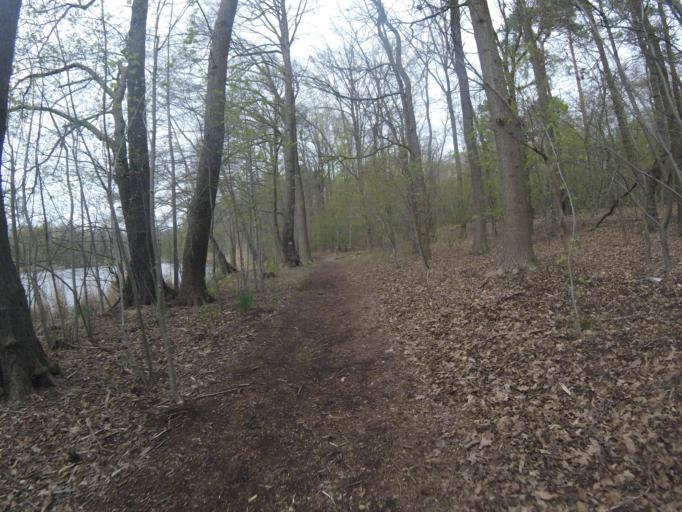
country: DE
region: Brandenburg
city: Konigs Wusterhausen
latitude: 52.2690
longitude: 13.6077
